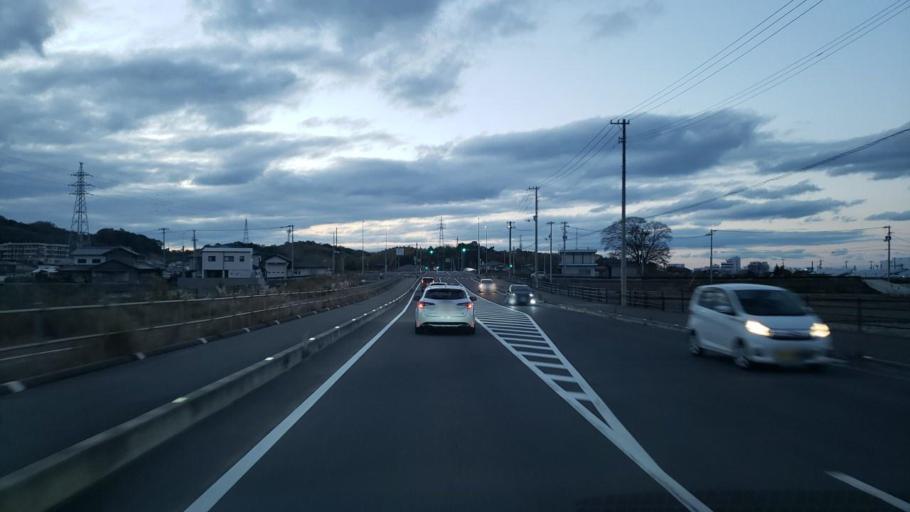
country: JP
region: Tokushima
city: Kamojimacho-jogejima
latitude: 34.2413
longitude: 134.3500
